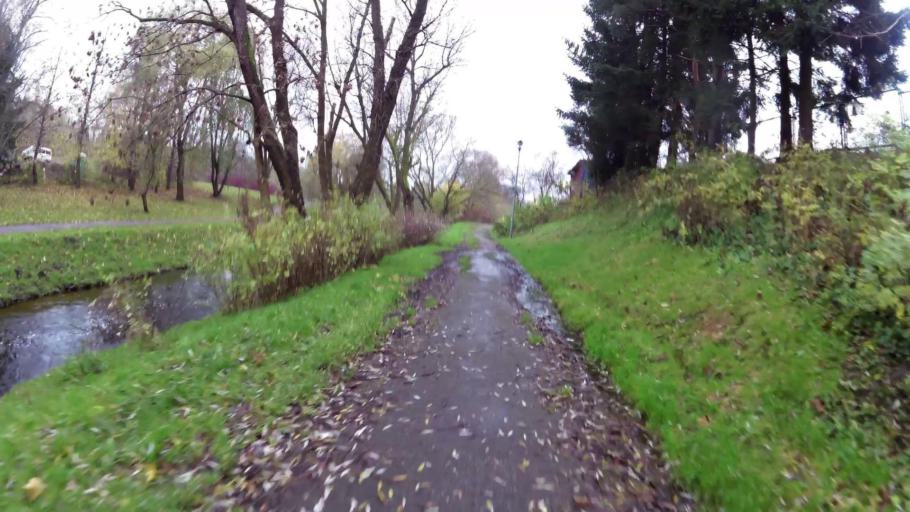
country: PL
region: West Pomeranian Voivodeship
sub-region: Koszalin
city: Koszalin
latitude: 54.1956
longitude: 16.1793
